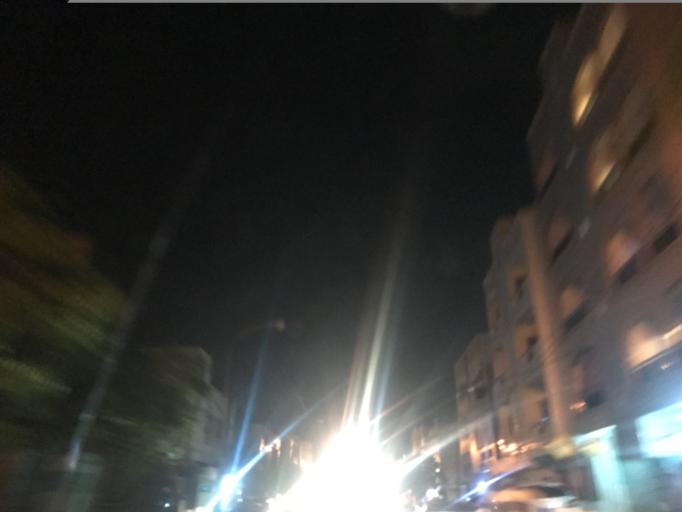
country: SN
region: Dakar
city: Grand Dakar
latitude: 14.7519
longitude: -17.4461
